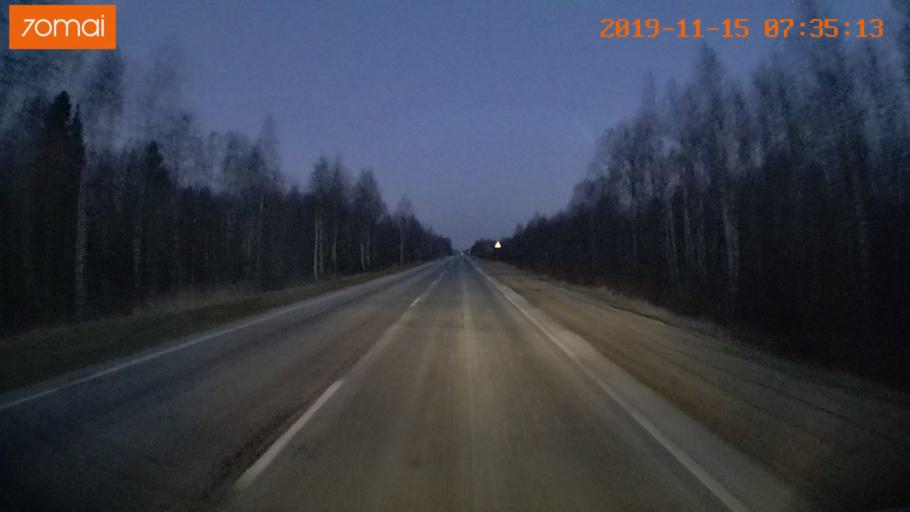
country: RU
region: Vologda
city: Sheksna
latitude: 58.7276
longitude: 38.4562
